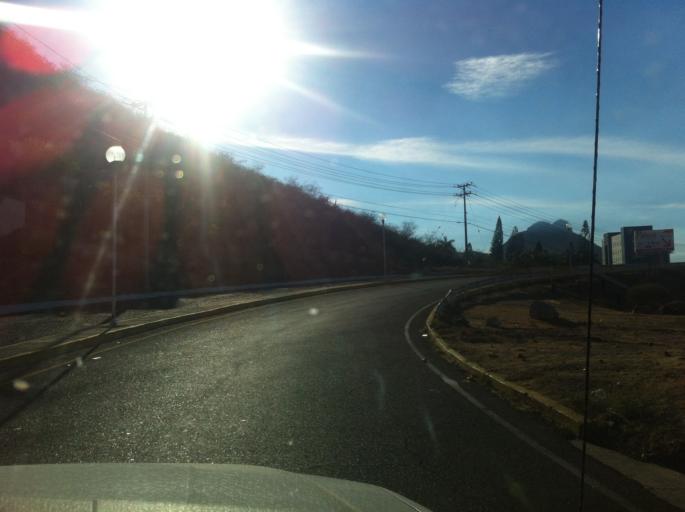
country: MX
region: Sonora
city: Heroica Guaymas
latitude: 27.9314
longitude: -110.9245
